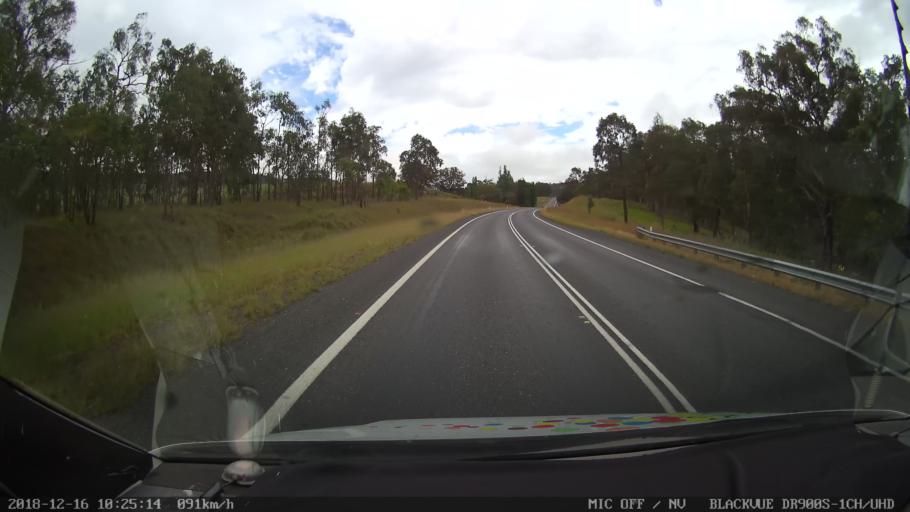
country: AU
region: New South Wales
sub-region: Tenterfield Municipality
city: Carrolls Creek
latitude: -29.1614
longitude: 152.0006
